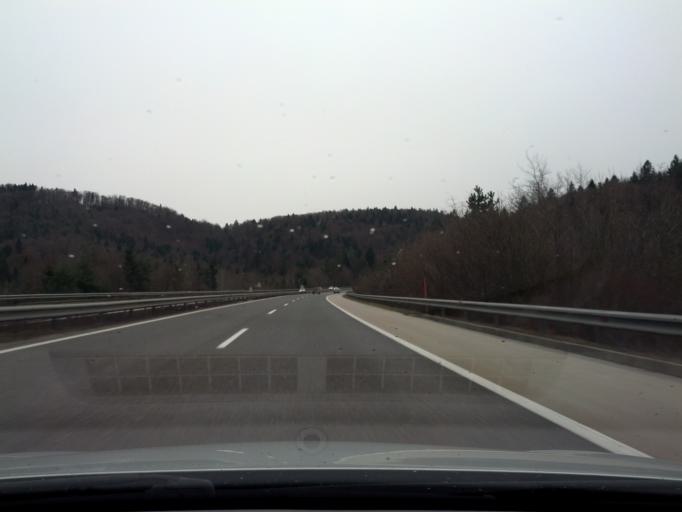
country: SI
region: Skofljica
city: Lavrica
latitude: 46.0032
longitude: 14.5767
